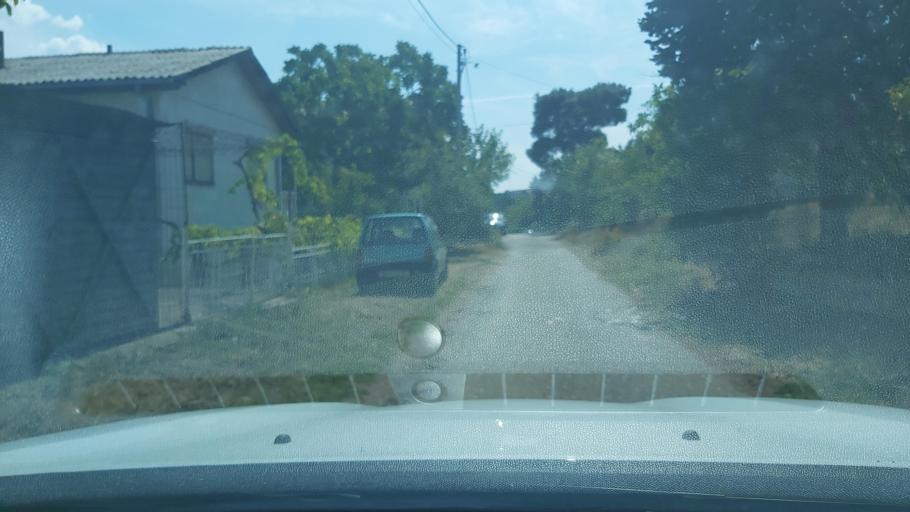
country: MK
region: Dojran
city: Star Dojran
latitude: 41.1818
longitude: 22.7218
